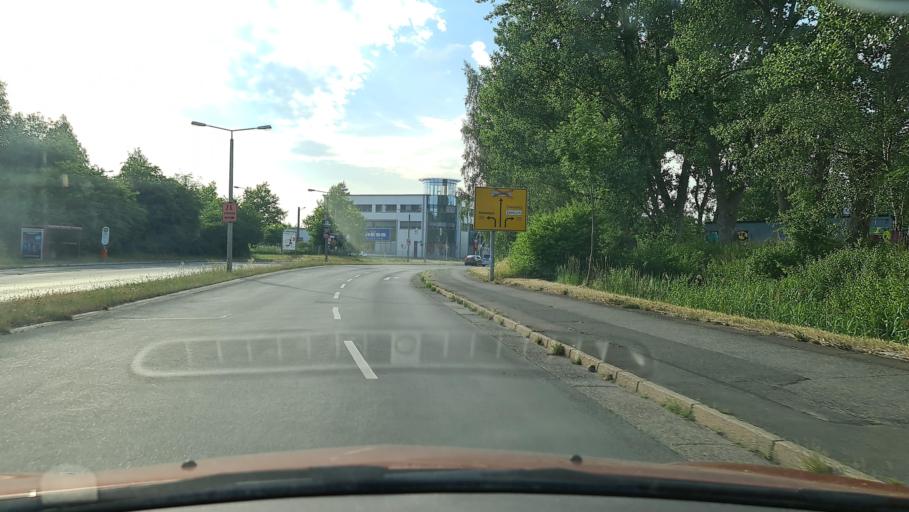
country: DE
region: Saxony
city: Lichtentanne
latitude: 50.7061
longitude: 12.4604
